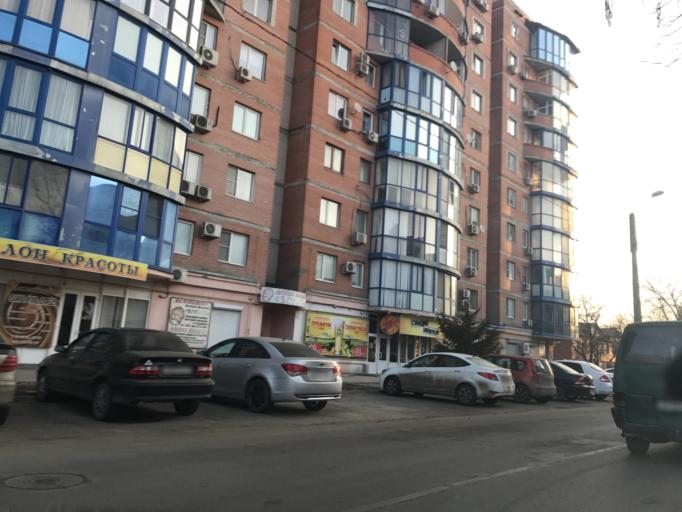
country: RU
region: Rostov
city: Rostov-na-Donu
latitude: 47.2147
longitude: 39.6644
